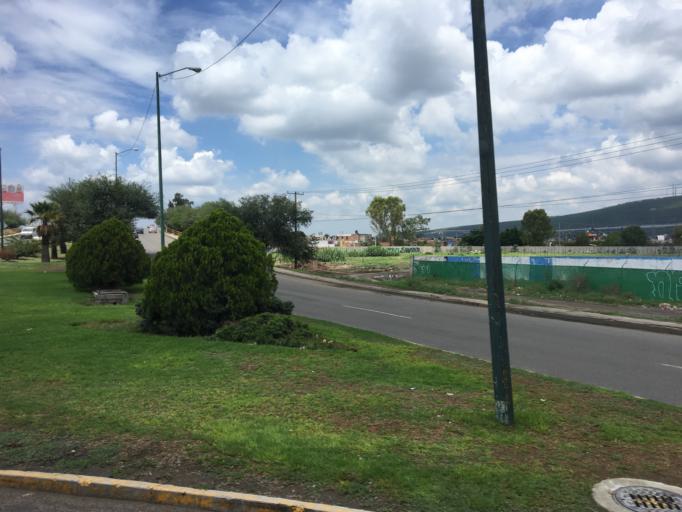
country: MX
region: Guanajuato
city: Irapuato
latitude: 20.7081
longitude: -101.3528
